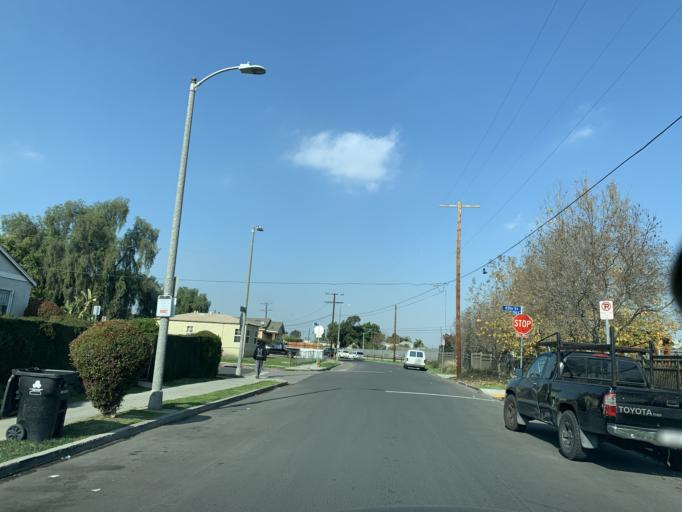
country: US
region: California
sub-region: Los Angeles County
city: Willowbrook
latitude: 33.9317
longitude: -118.2402
